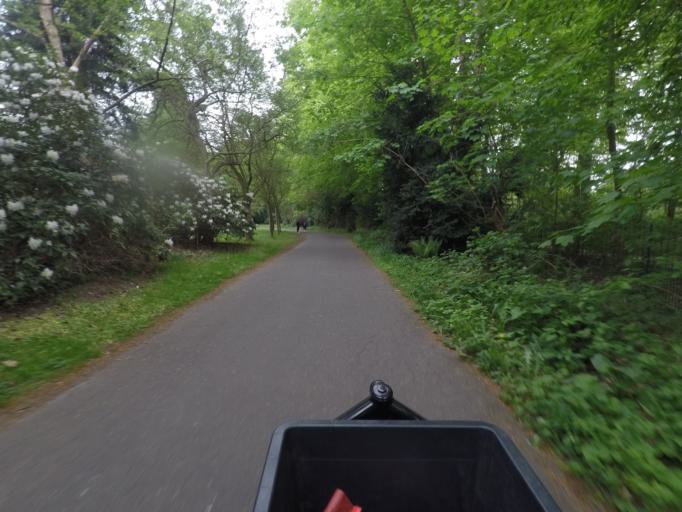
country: DE
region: Hamburg
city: Steilshoop
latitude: 53.6202
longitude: 10.0663
